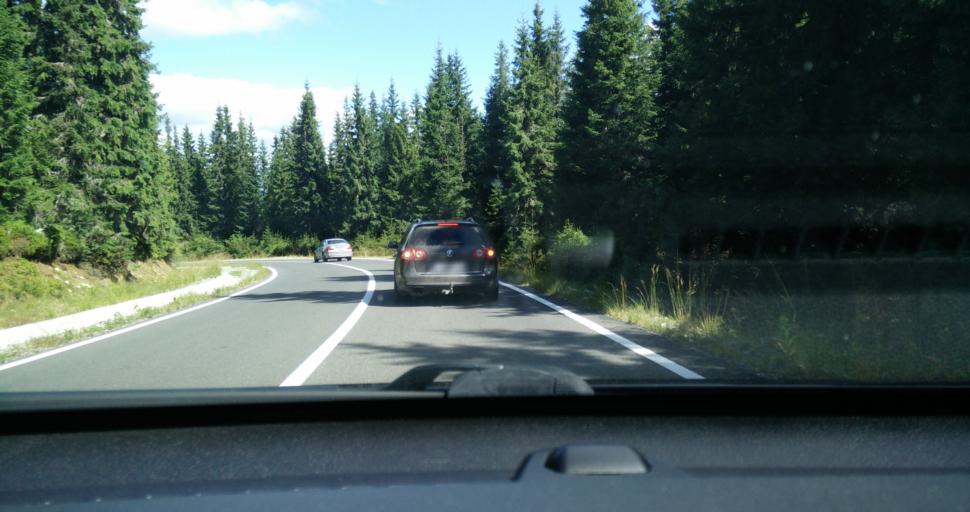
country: RO
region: Hunedoara
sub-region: Oras Petrila
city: Petrila
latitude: 45.4768
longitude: 23.6406
